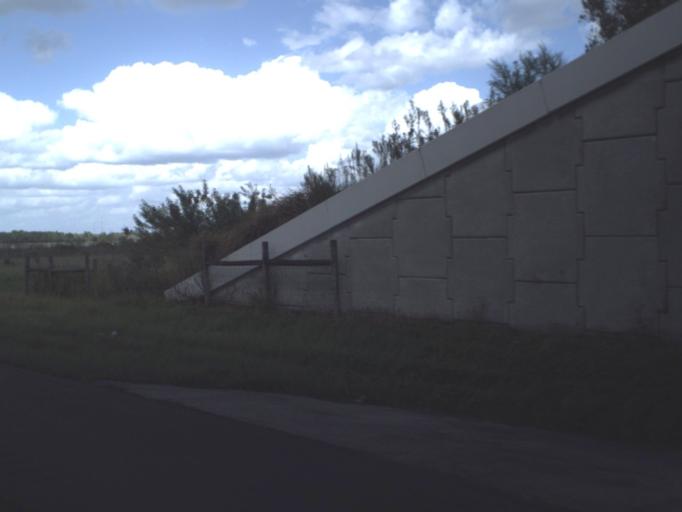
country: US
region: Florida
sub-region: Polk County
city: Fussels Corner
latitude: 28.0404
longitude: -81.8337
